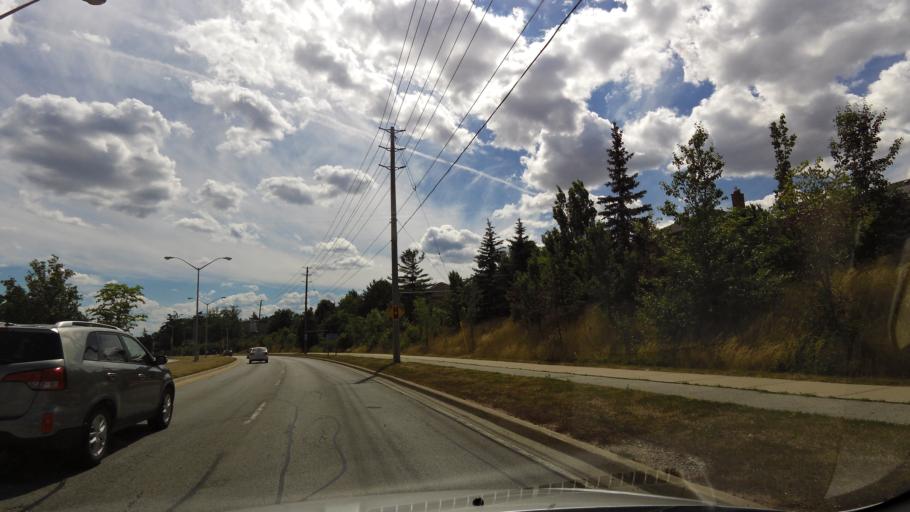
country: CA
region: Ontario
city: Oakville
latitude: 43.4621
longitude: -79.7185
